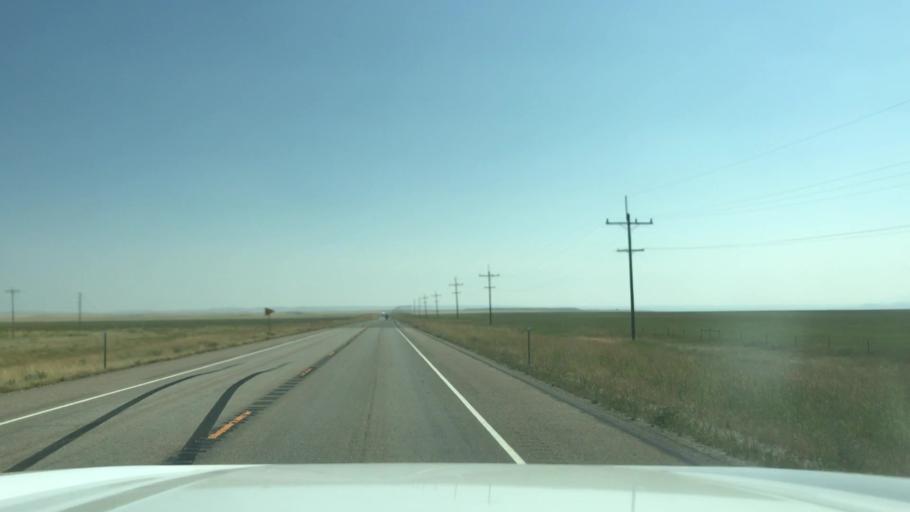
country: US
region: Montana
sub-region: Wheatland County
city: Harlowton
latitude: 46.5214
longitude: -109.7661
